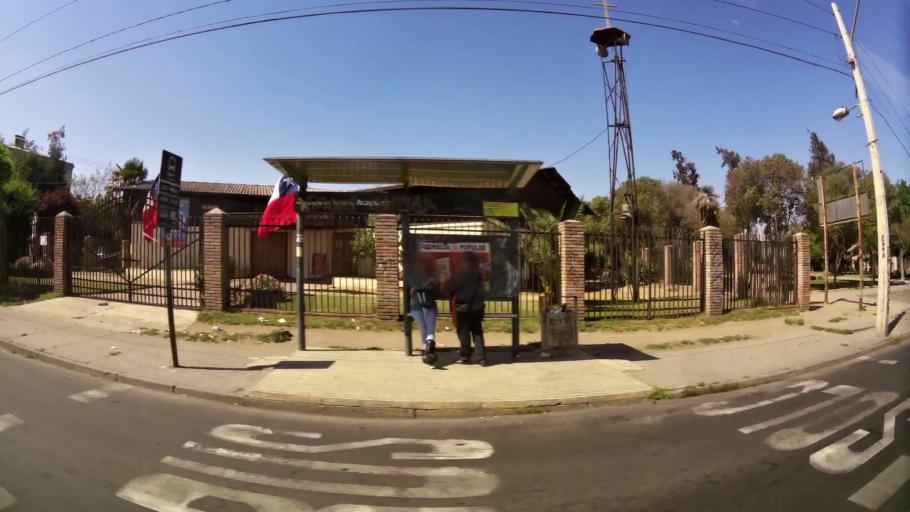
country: CL
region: Santiago Metropolitan
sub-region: Provincia de Santiago
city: Lo Prado
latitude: -33.5067
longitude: -70.7350
